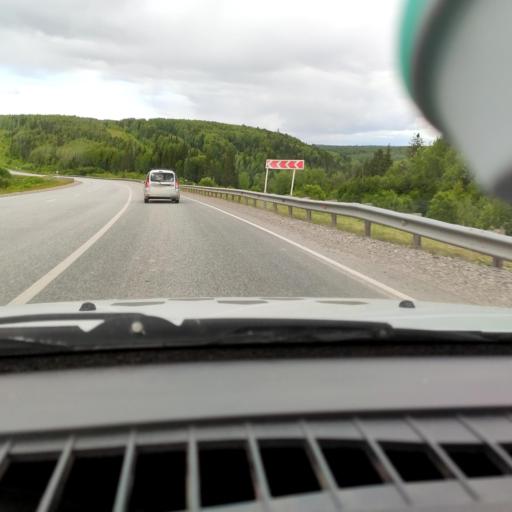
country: RU
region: Perm
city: Polazna
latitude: 58.2888
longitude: 56.5050
